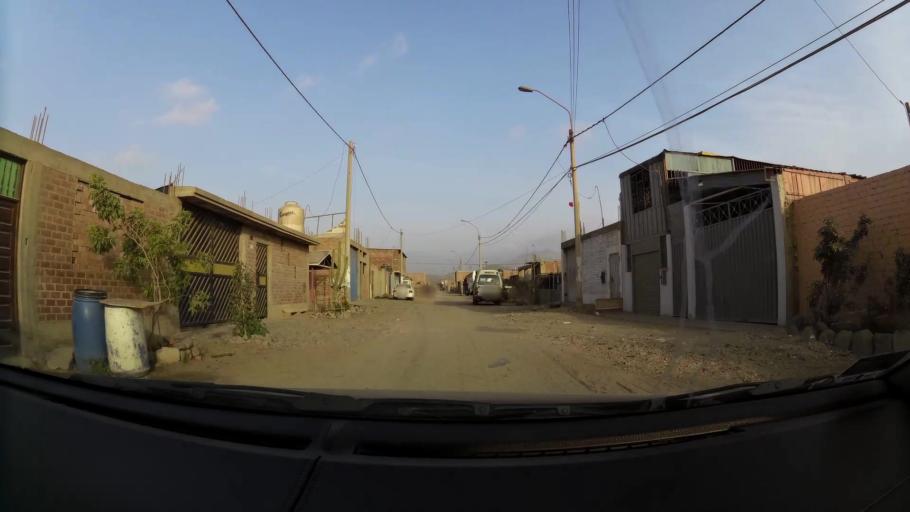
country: PE
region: Lima
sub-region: Lima
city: Santa Rosa
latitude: -11.7459
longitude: -77.1489
